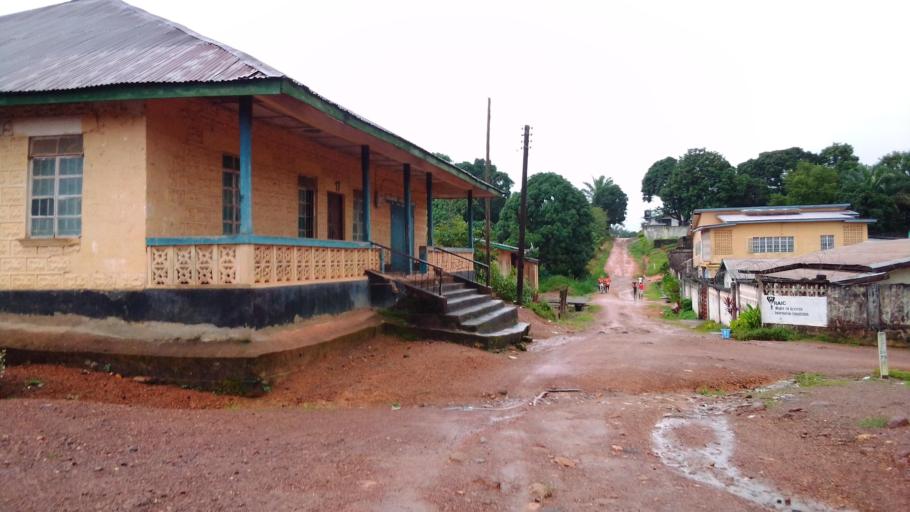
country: SL
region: Eastern Province
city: Kenema
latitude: 7.8904
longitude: -11.1904
